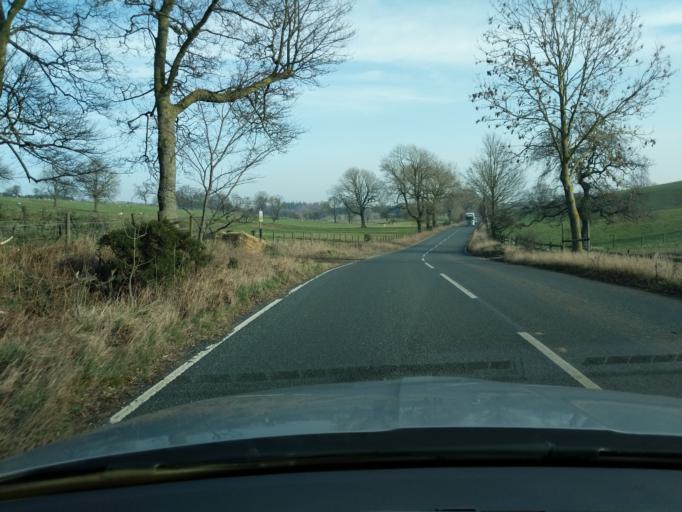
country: GB
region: England
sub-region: North Yorkshire
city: Catterick Garrison
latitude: 54.3475
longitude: -1.7523
